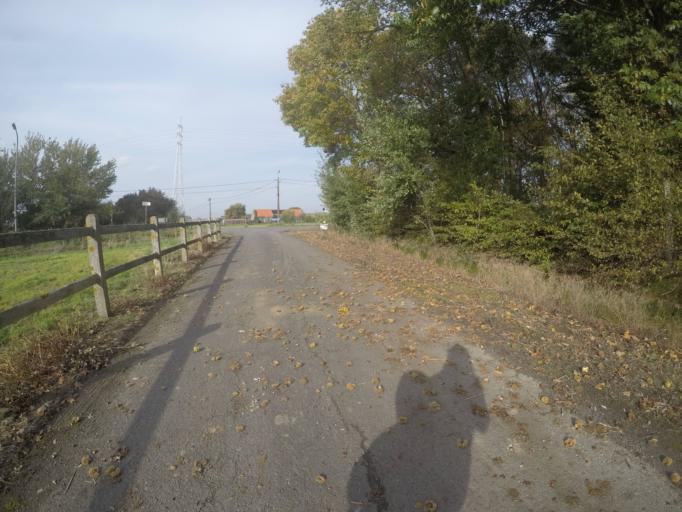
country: BE
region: Flanders
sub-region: Provincie West-Vlaanderen
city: Wervik
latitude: 50.8285
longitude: 3.0497
